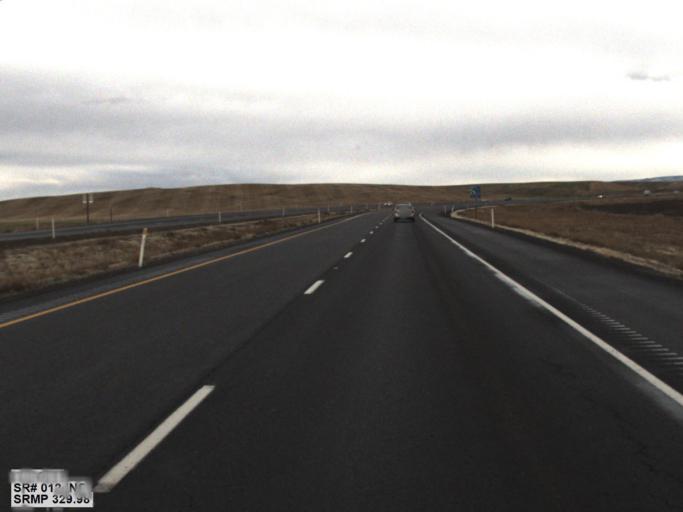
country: US
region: Washington
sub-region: Walla Walla County
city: Garrett
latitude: 46.0522
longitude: -118.4720
